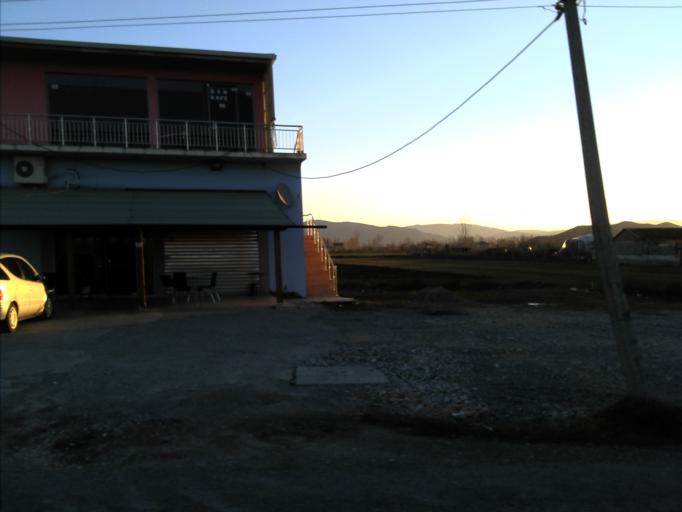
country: AL
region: Shkoder
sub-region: Rrethi i Shkodres
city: Berdica e Madhe
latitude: 41.9861
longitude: 19.4799
